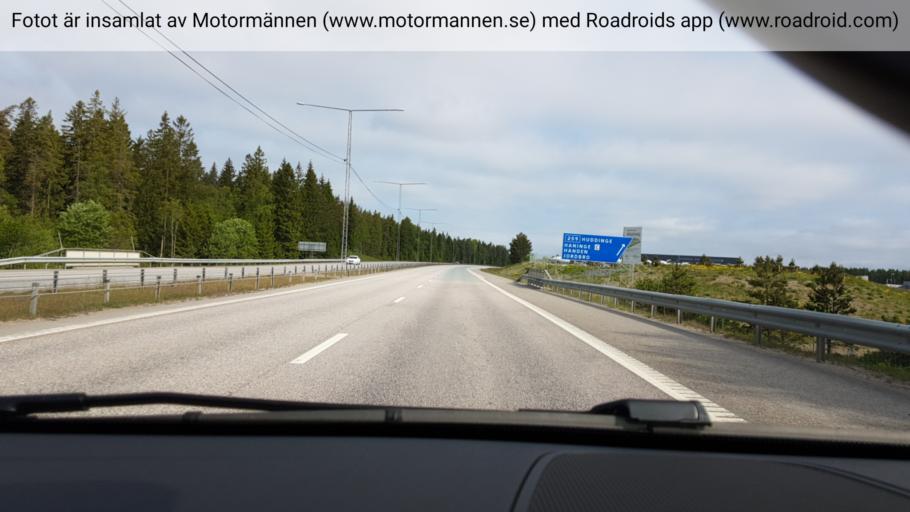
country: SE
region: Stockholm
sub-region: Haninge Kommun
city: Haninge
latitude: 59.1464
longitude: 18.1592
